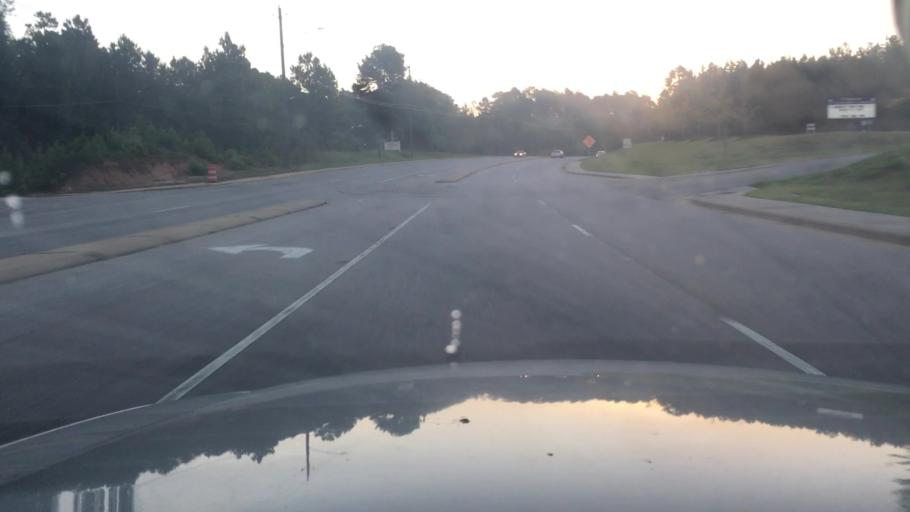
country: US
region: North Carolina
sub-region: Hoke County
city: Rockfish
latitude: 35.0640
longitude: -79.0375
